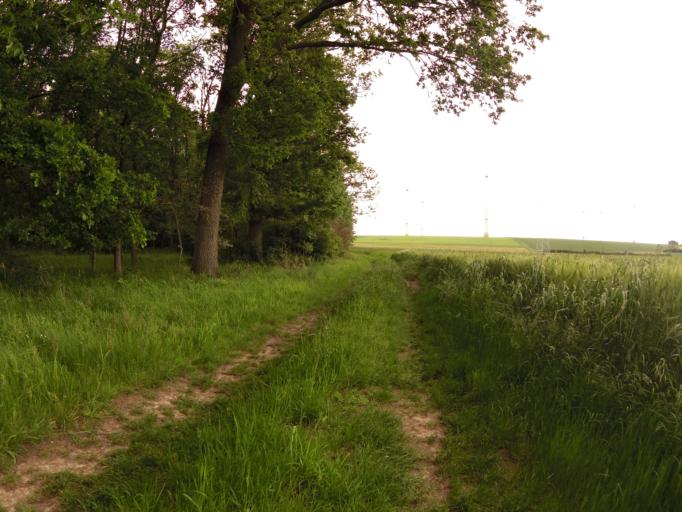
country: DE
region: Bavaria
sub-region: Regierungsbezirk Unterfranken
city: Theilheim
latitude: 49.7296
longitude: 10.0510
